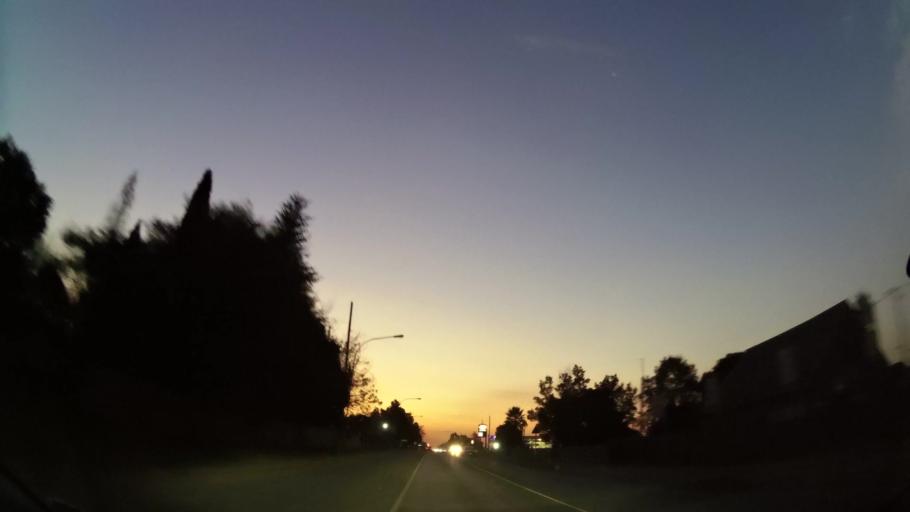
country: ZA
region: Gauteng
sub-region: Ekurhuleni Metropolitan Municipality
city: Benoni
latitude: -26.0961
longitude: 28.3098
